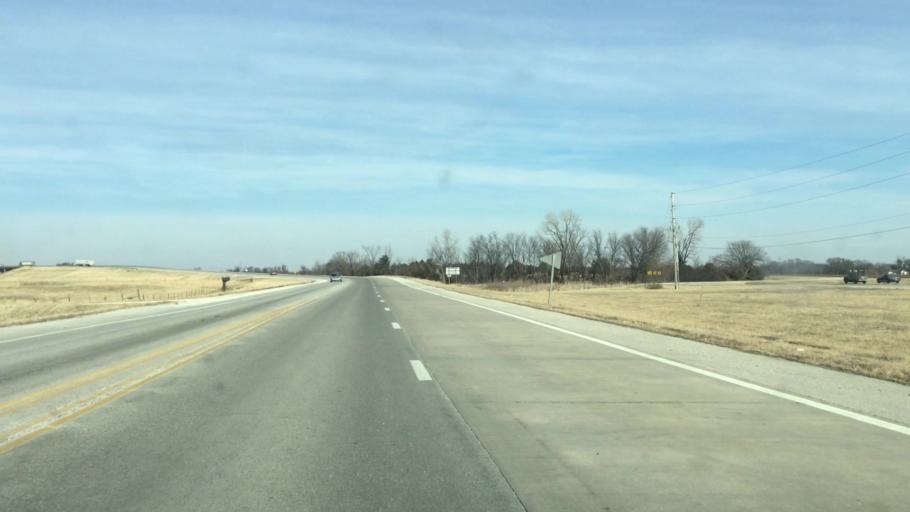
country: US
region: Kansas
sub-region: Labette County
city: Parsons
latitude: 37.3768
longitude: -95.2584
